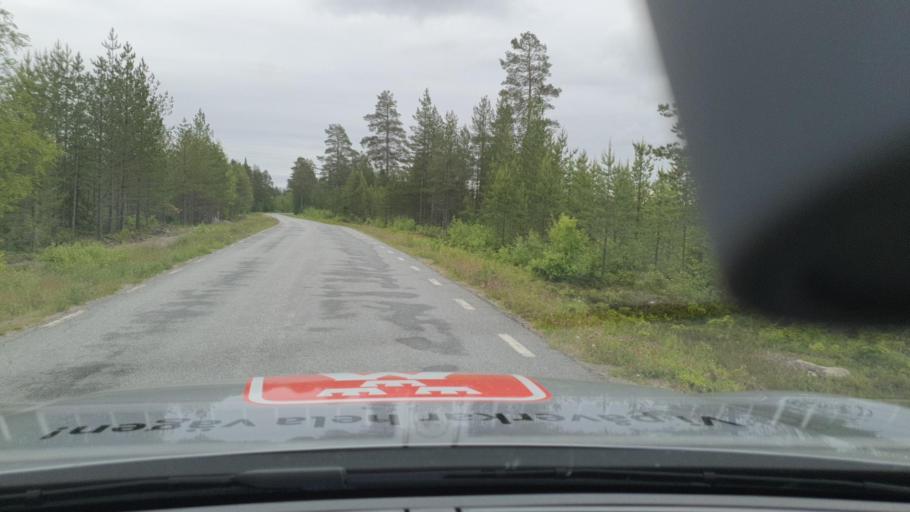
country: SE
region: Norrbotten
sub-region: Lulea Kommun
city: Ranea
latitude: 65.8335
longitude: 22.3095
